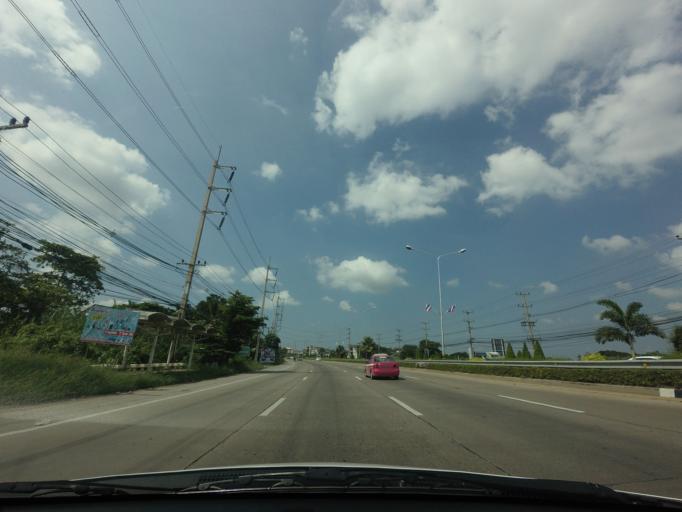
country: TH
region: Nakhon Pathom
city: Sam Phran
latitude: 13.7462
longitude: 100.2271
